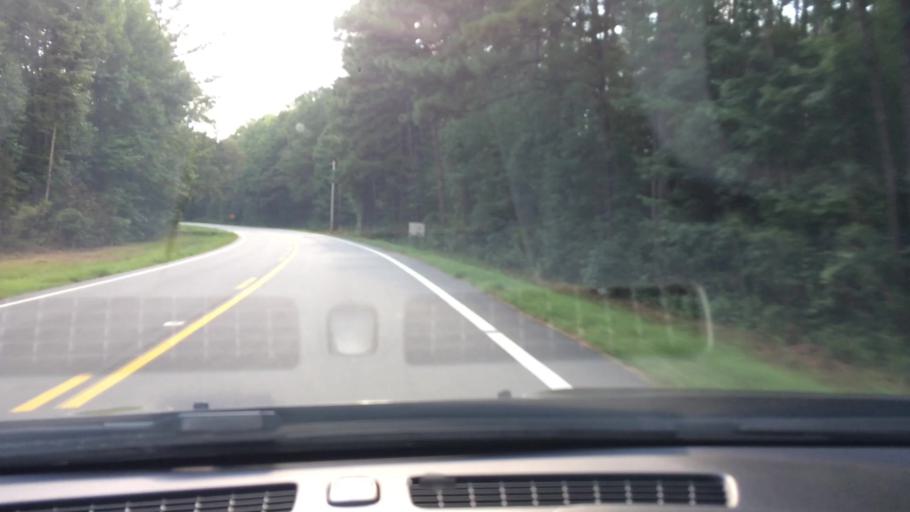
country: US
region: North Carolina
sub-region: Craven County
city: Vanceboro
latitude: 35.4194
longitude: -77.2511
